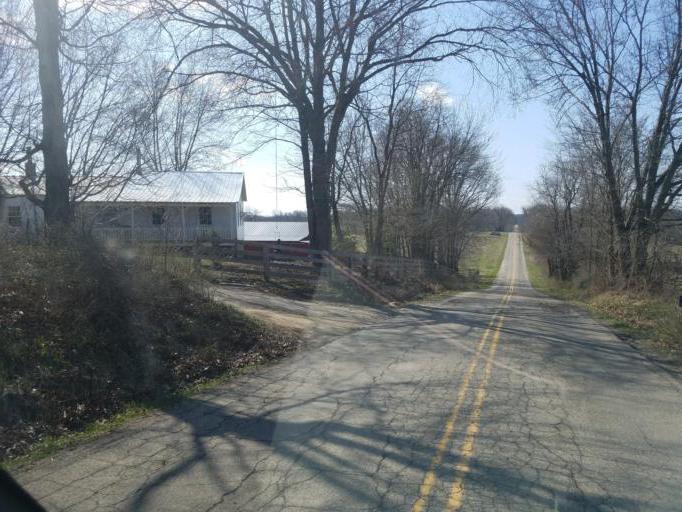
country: US
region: Ohio
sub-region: Licking County
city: Utica
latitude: 40.2600
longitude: -82.3220
